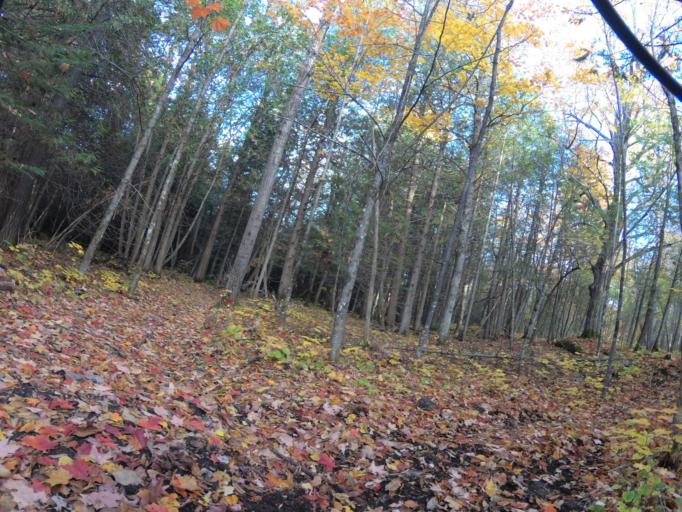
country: CA
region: Ontario
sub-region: Lanark County
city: Smiths Falls
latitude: 45.0318
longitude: -75.8046
